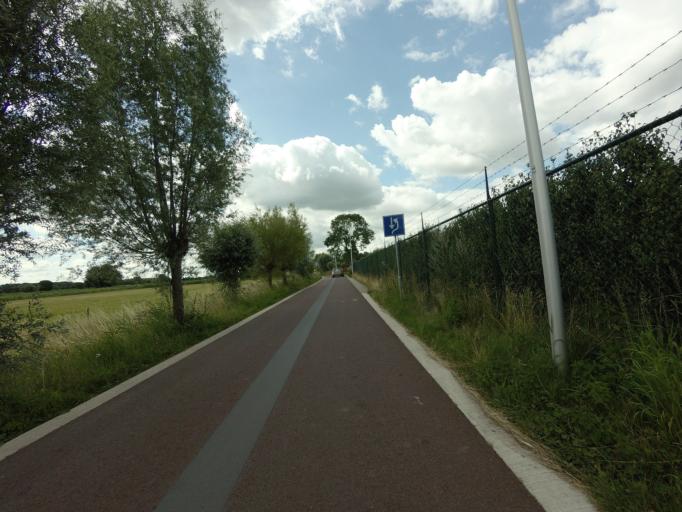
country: NL
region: Utrecht
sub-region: Gemeente Utrecht
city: Lunetten
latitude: 52.0406
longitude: 5.1263
